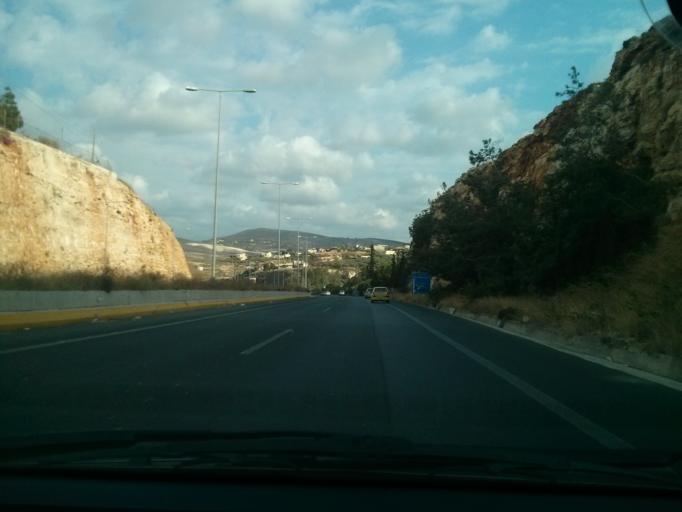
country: GR
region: Crete
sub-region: Nomos Irakleiou
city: Nea Alikarnassos
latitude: 35.3240
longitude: 25.1813
